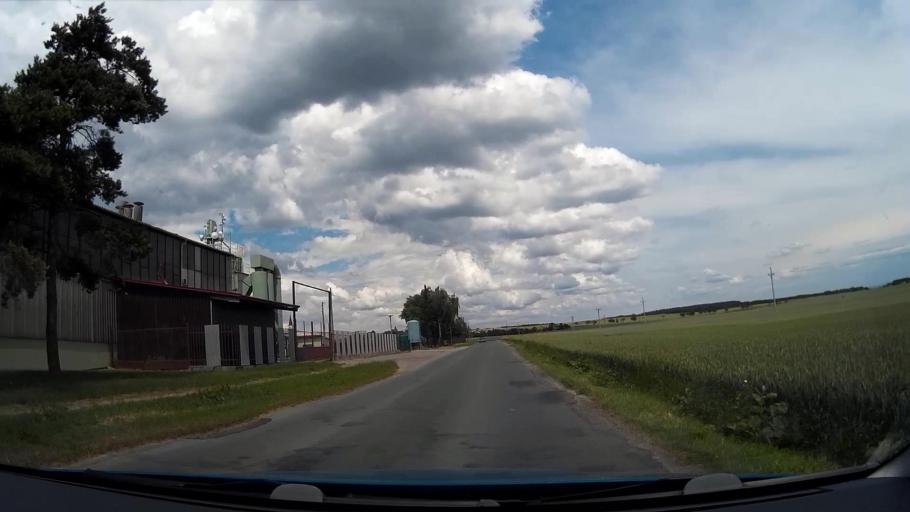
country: CZ
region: South Moravian
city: Orechov
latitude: 49.1054
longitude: 16.5255
